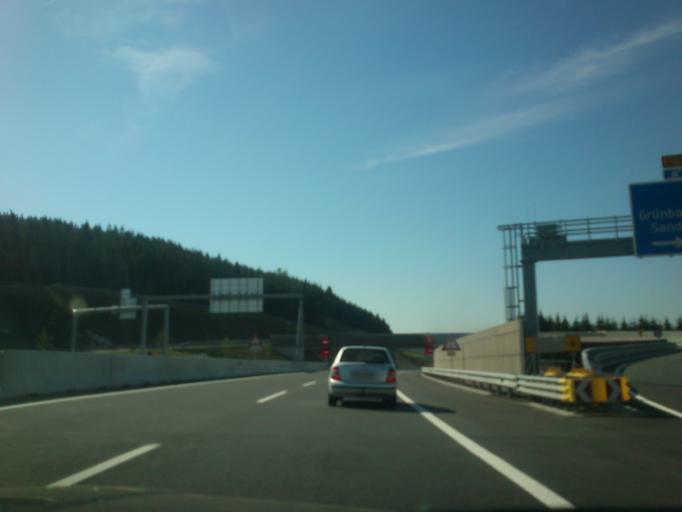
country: AT
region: Upper Austria
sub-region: Politischer Bezirk Freistadt
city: Freistadt
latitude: 48.5177
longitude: 14.5157
